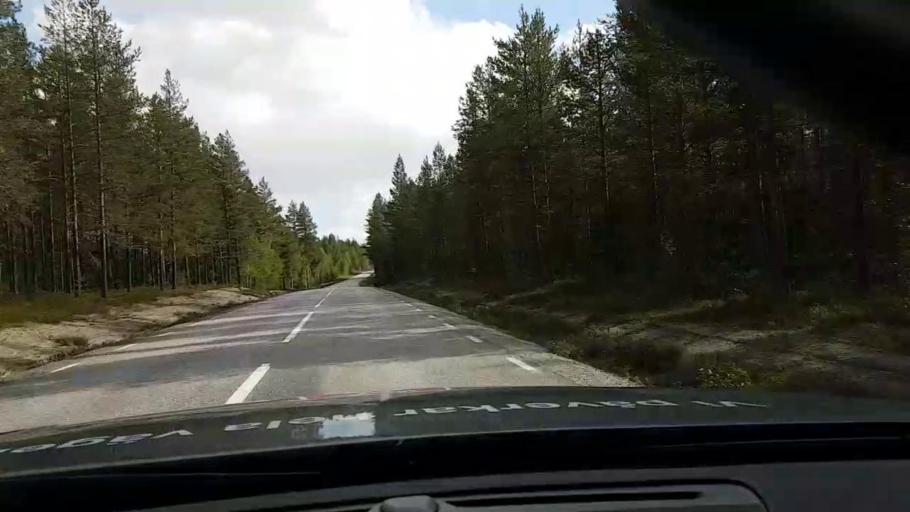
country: SE
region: Vaesternorrland
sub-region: OErnskoeldsviks Kommun
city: Bredbyn
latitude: 63.6517
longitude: 17.8885
